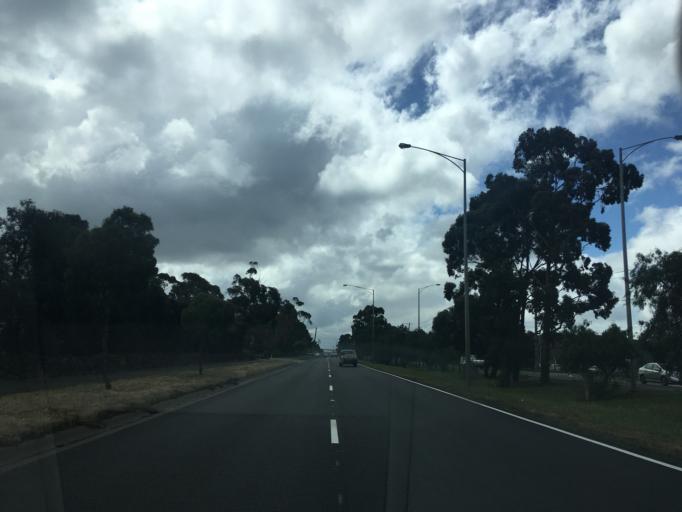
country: AU
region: Victoria
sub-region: Brimbank
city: Derrimut
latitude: -37.8197
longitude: 144.7865
